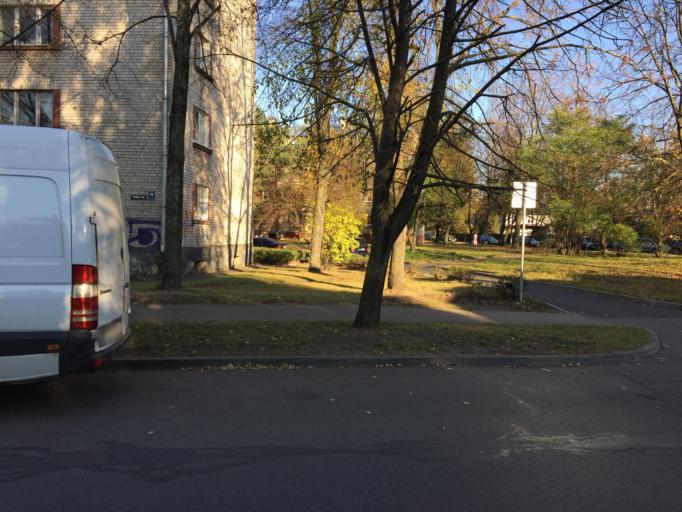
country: LV
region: Marupe
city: Marupe
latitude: 56.9426
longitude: 24.0598
